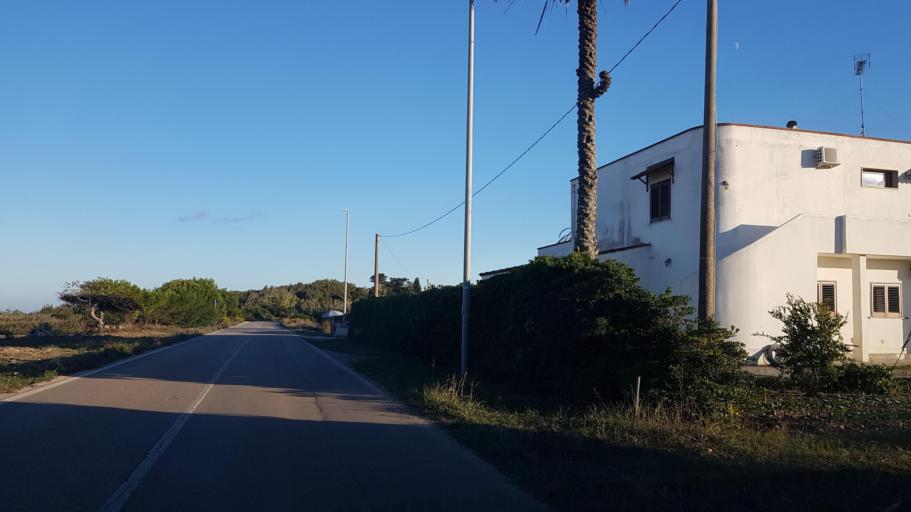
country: IT
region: Apulia
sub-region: Provincia di Lecce
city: Giorgilorio
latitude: 40.4477
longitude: 18.2284
